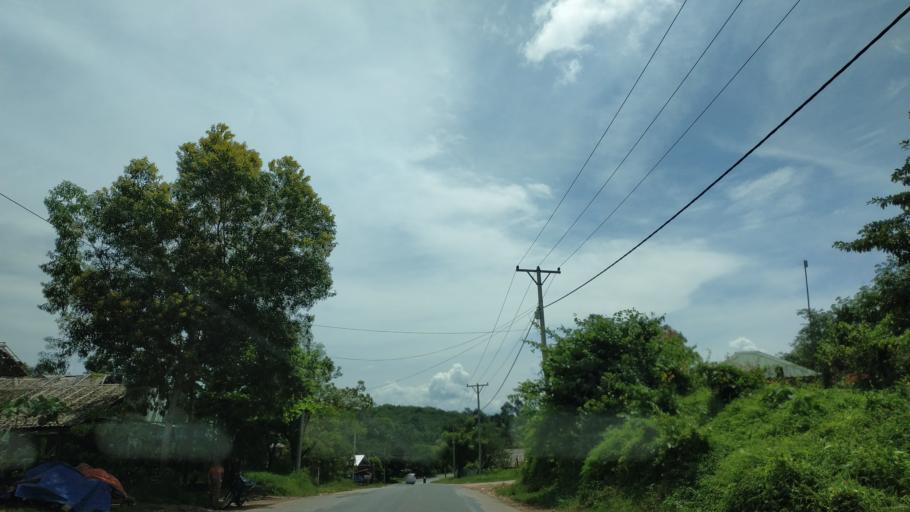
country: MM
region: Tanintharyi
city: Dawei
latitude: 14.1109
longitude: 98.1620
